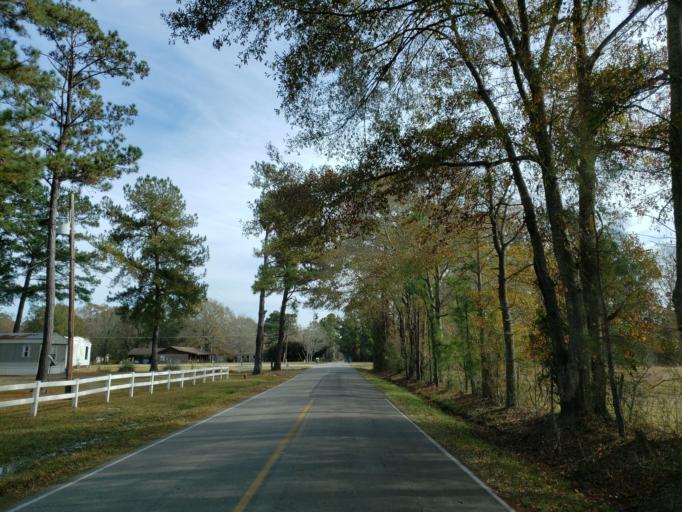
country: US
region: Mississippi
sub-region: Forrest County
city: Rawls Springs
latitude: 31.3993
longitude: -89.3925
